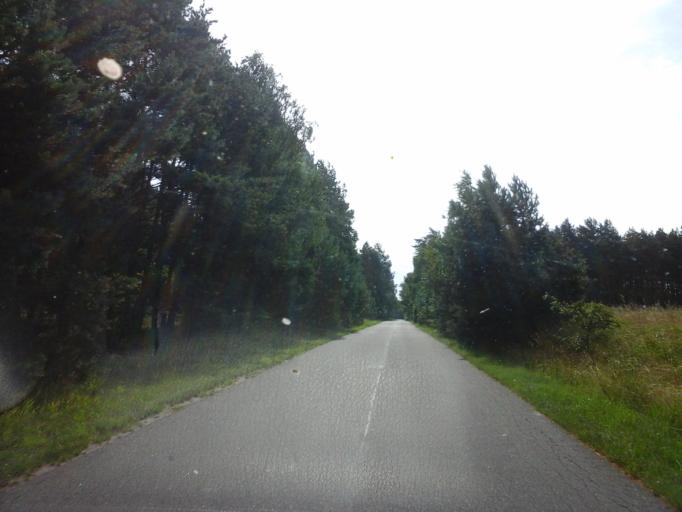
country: PL
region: West Pomeranian Voivodeship
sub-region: Powiat choszczenski
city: Bierzwnik
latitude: 53.0451
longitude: 15.6319
